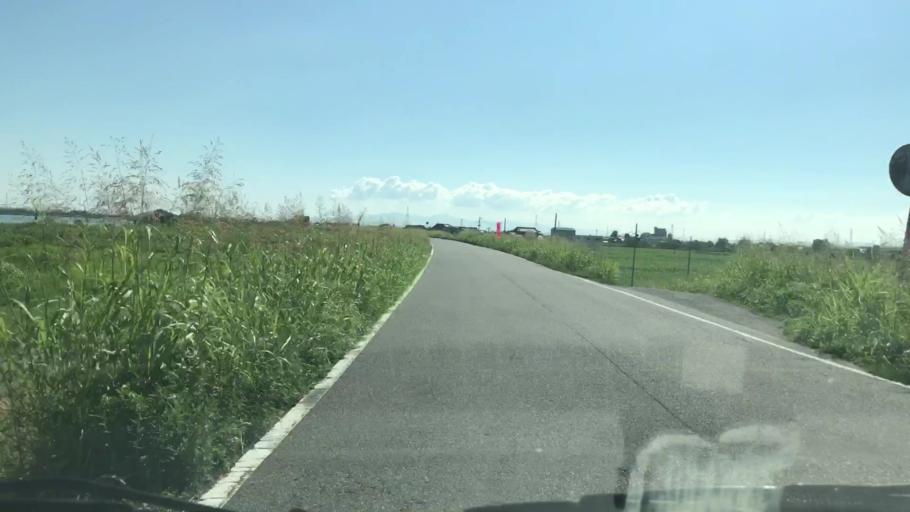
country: JP
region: Saga Prefecture
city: Kanzakimachi-kanzaki
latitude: 33.2693
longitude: 130.4234
